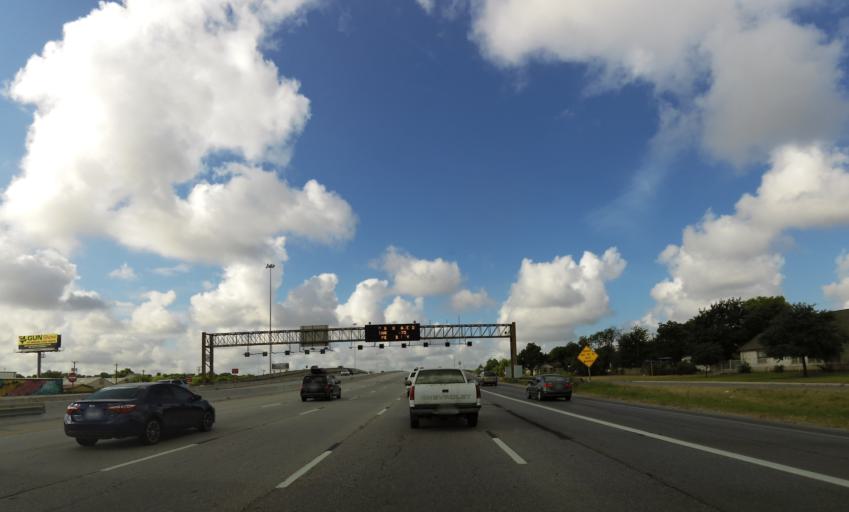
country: US
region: Texas
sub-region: Bexar County
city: Olmos Park
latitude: 29.4640
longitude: -98.5161
